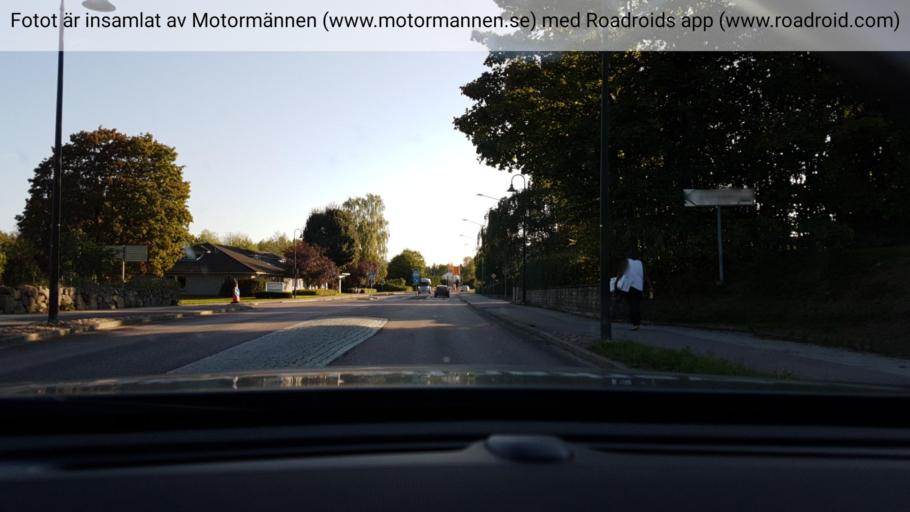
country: SE
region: Joenkoeping
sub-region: Gislaveds Kommun
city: Smalandsstenar
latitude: 57.1607
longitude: 13.4109
